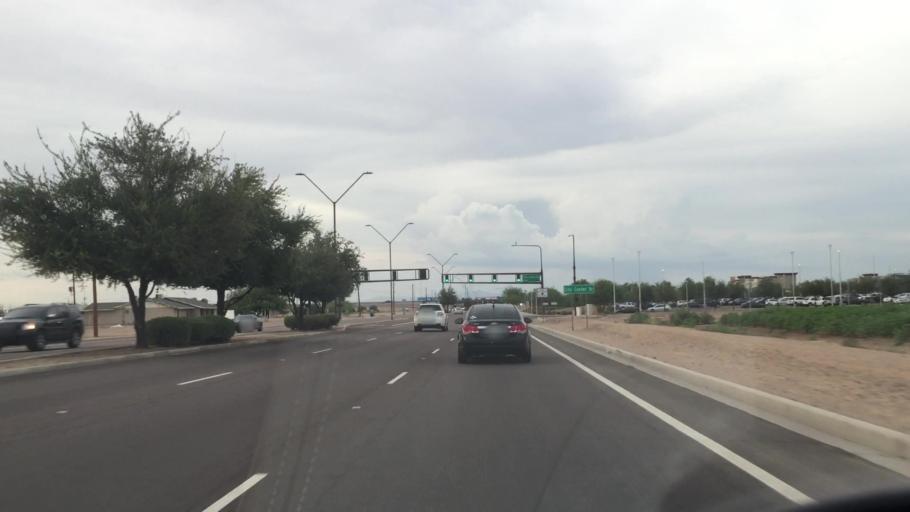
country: US
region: Arizona
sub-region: Maricopa County
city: Avondale
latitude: 33.4514
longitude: -112.3064
